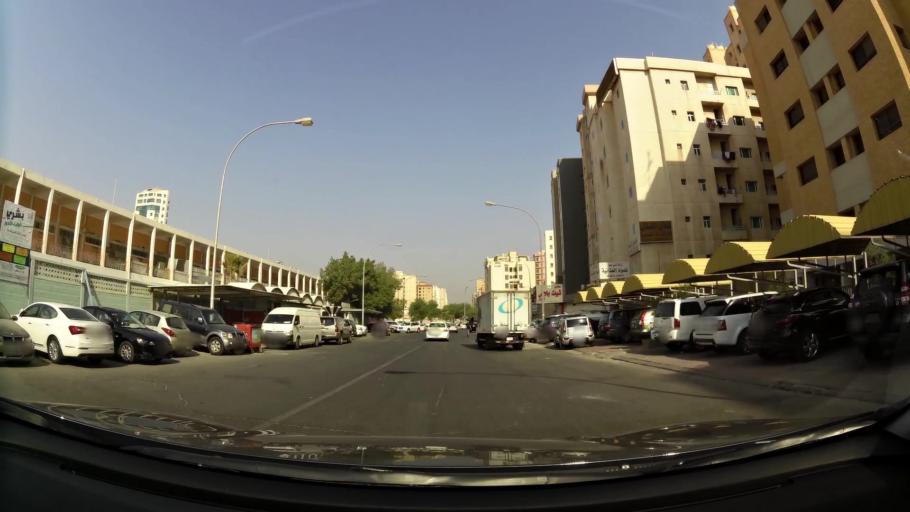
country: KW
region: Muhafazat Hawalli
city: Hawalli
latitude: 29.3244
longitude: 48.0146
